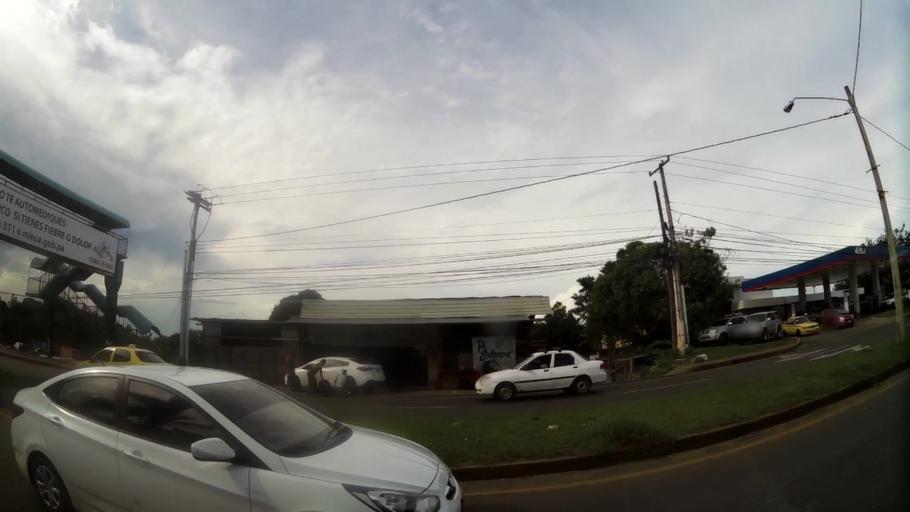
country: PA
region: Panama
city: La Chorrera
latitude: 8.8741
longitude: -79.7921
